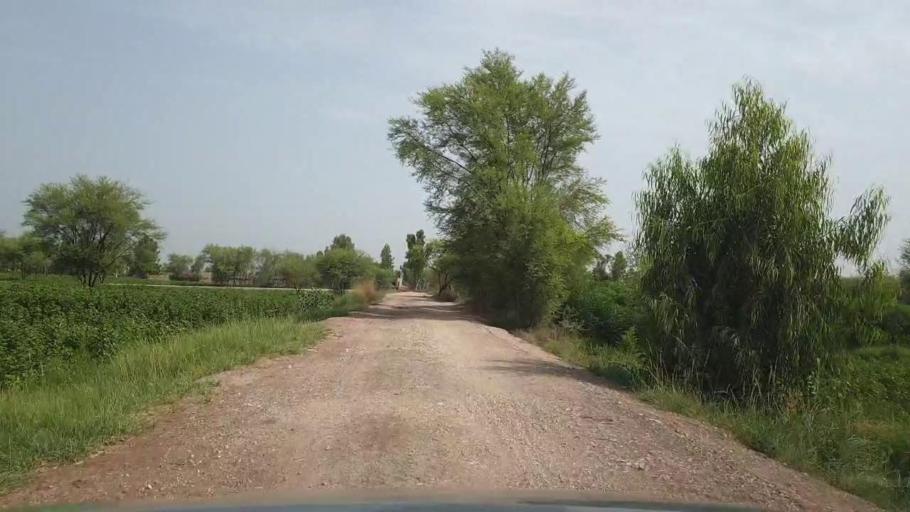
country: PK
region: Sindh
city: Rohri
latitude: 27.6564
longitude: 69.0244
